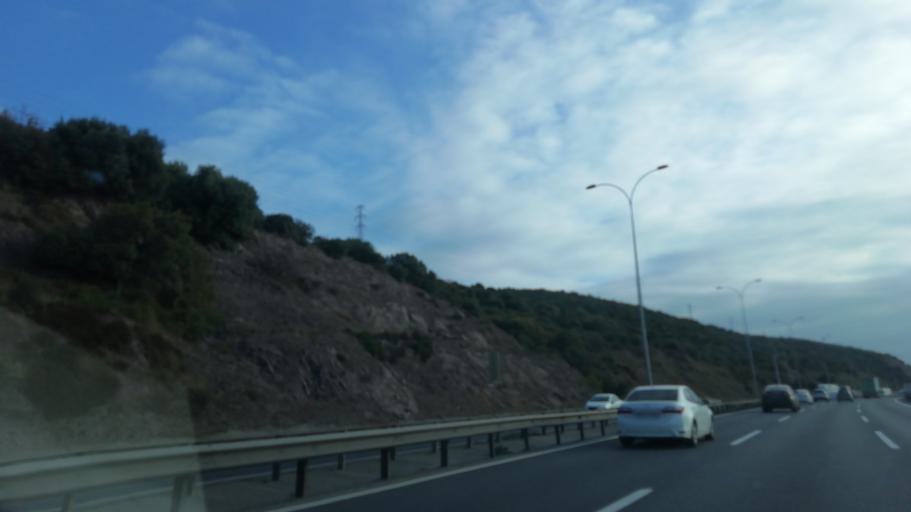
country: TR
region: Kocaeli
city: Hereke
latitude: 40.7799
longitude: 29.6657
